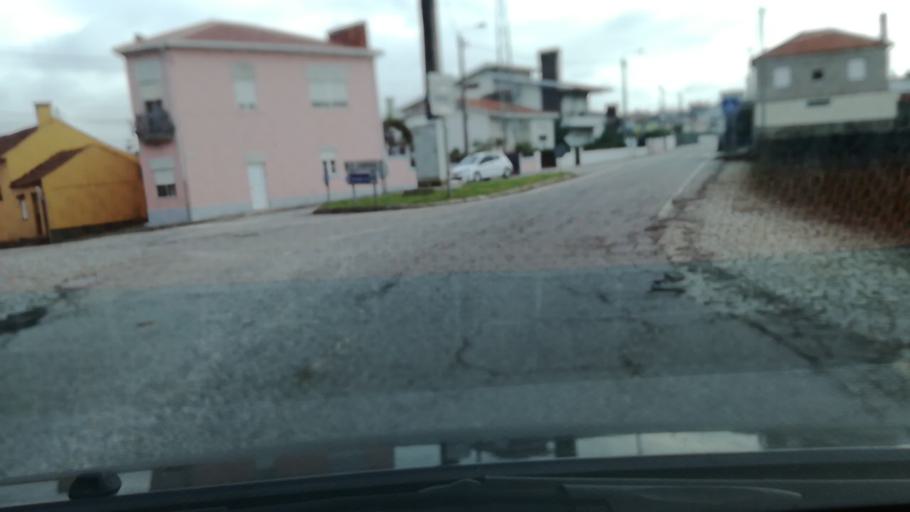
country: PT
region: Porto
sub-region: Maia
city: Gemunde
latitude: 41.2677
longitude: -8.6522
